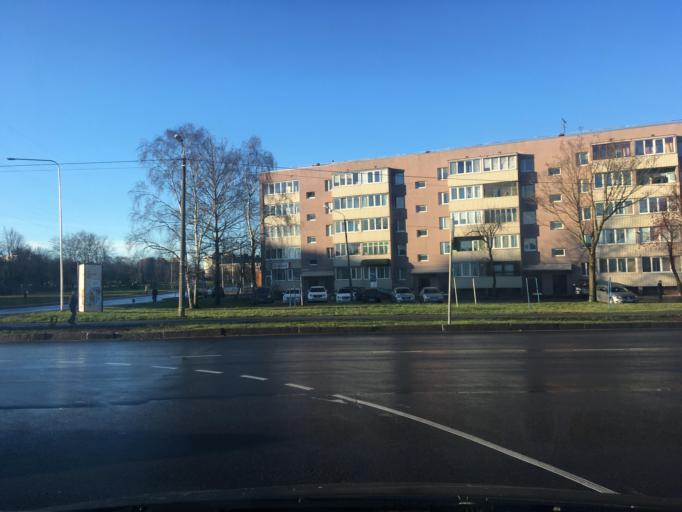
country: EE
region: Ida-Virumaa
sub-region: Narva linn
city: Narva
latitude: 59.3877
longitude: 28.1749
